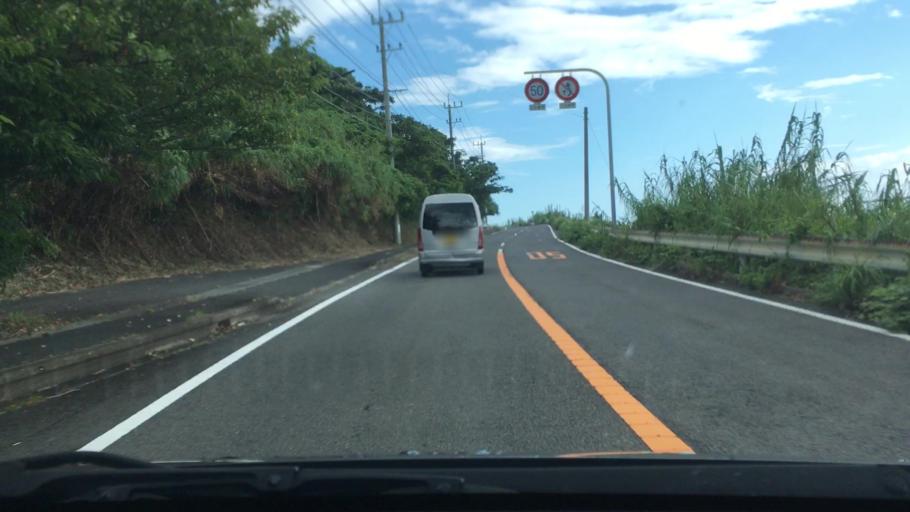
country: JP
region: Nagasaki
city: Togitsu
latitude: 32.8725
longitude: 129.6785
